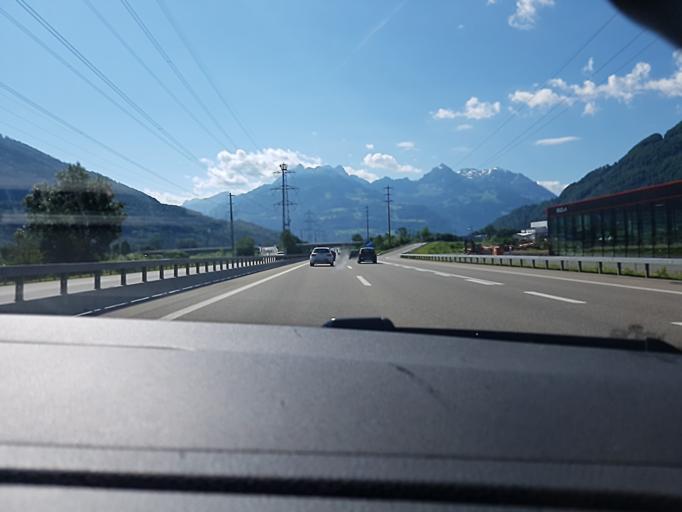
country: CH
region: Glarus
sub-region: Glarus
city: Bilten
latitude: 47.1555
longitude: 9.0297
